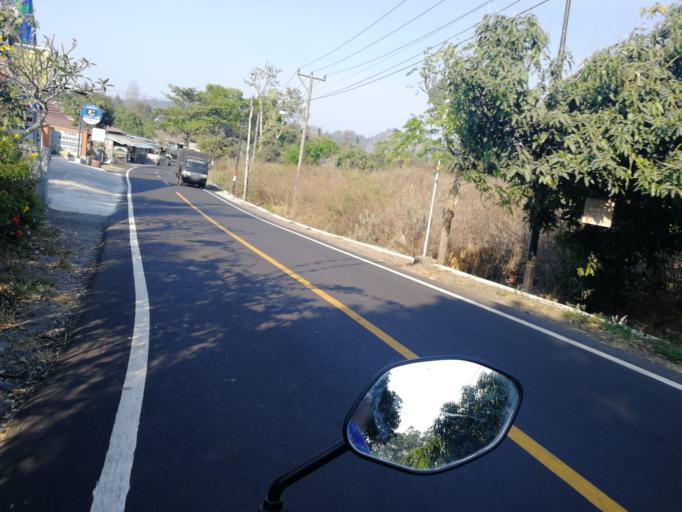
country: ID
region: Bali
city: Banjar Trunyan
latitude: -8.2509
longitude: 115.3966
